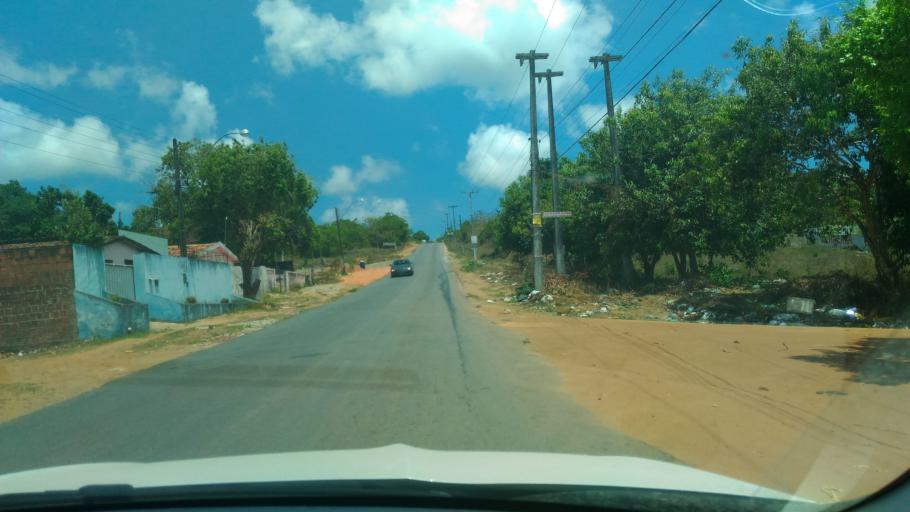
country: BR
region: Paraiba
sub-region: Conde
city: Conde
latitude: -7.2611
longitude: -34.9159
